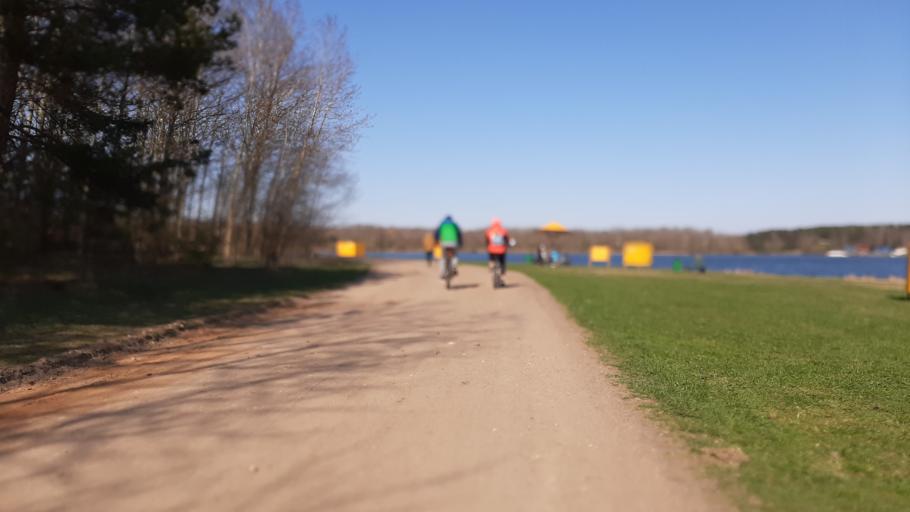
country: BY
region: Minsk
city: Bal'shavik
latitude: 53.9549
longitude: 27.5763
